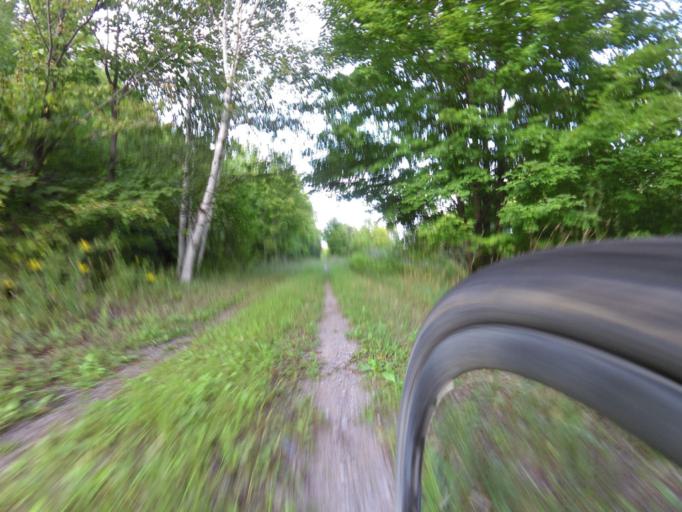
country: CA
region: Ontario
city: Gananoque
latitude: 44.5535
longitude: -76.3822
